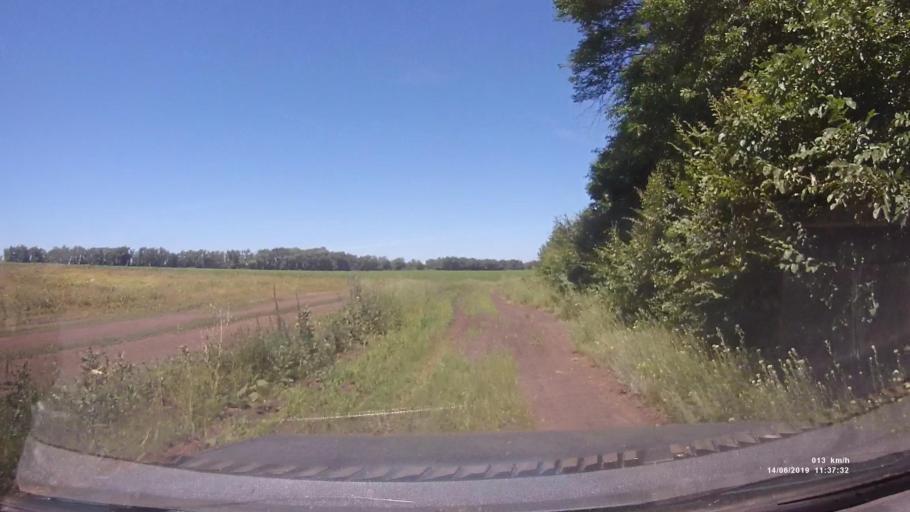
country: RU
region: Rostov
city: Kazanskaya
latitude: 49.8632
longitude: 41.3719
